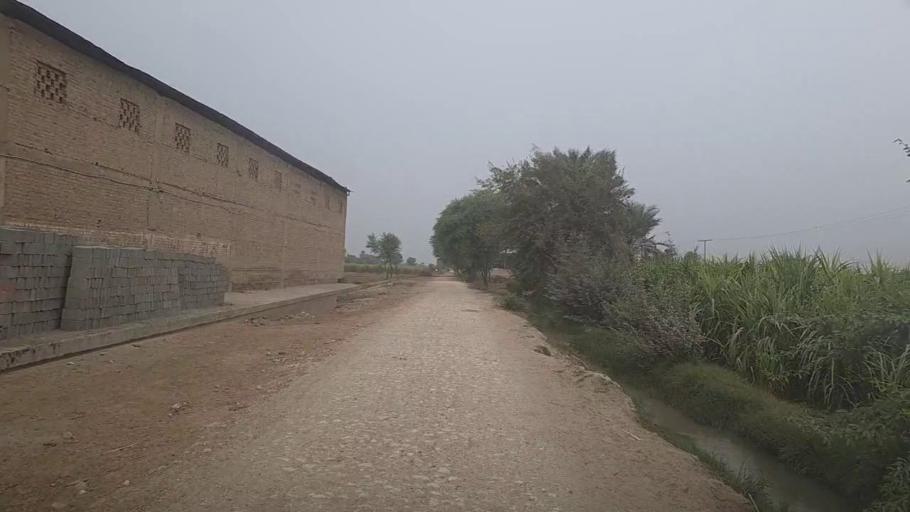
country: PK
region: Sindh
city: Gambat
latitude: 27.3010
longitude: 68.6056
